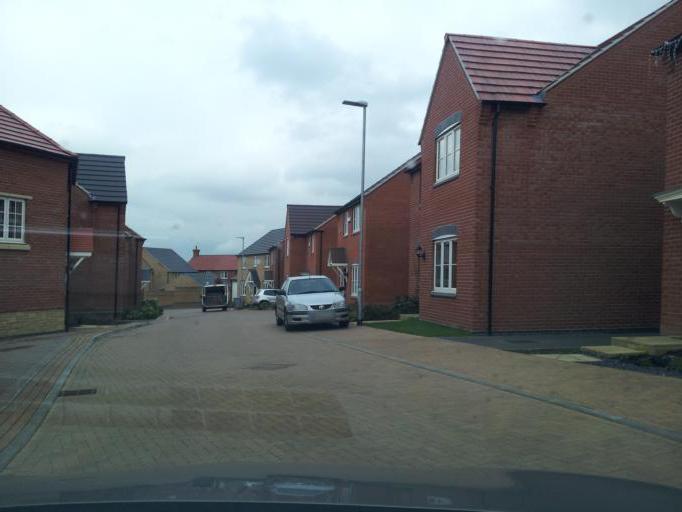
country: GB
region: England
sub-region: Lincolnshire
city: Great Gonerby
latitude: 52.9196
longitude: -0.6619
